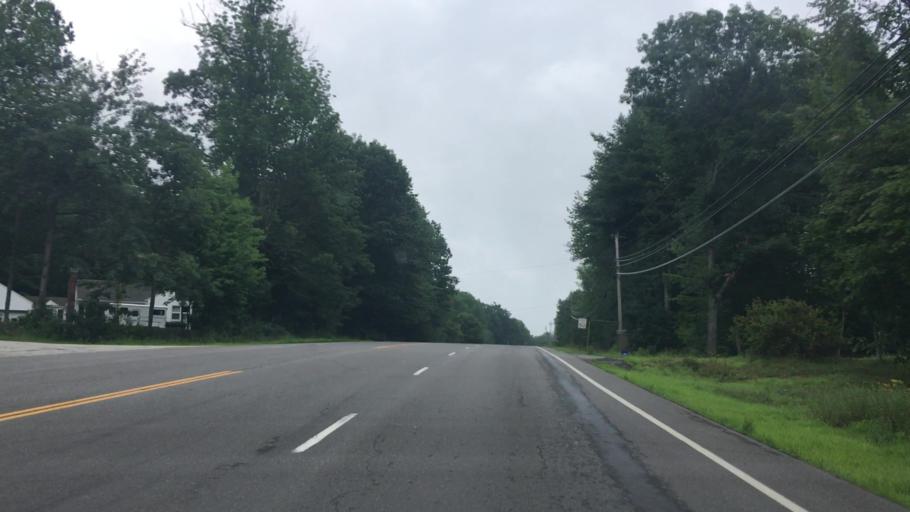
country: US
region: Maine
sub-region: York County
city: Sanford (historical)
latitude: 43.4259
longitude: -70.8123
